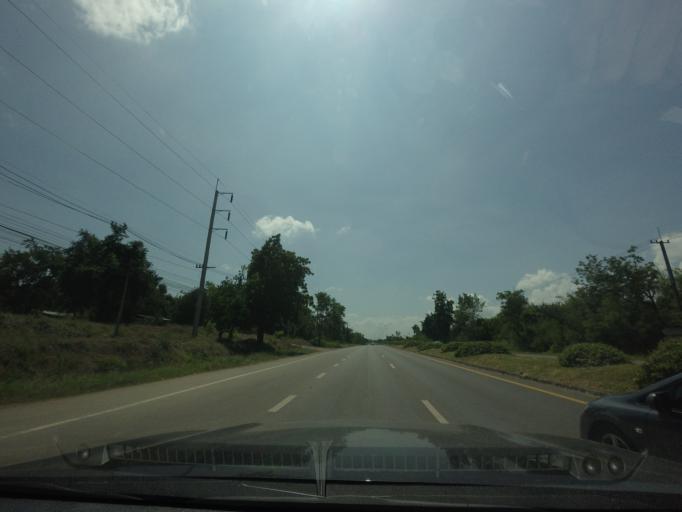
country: TH
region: Phetchabun
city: Lom Sak
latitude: 16.6750
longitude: 101.1608
